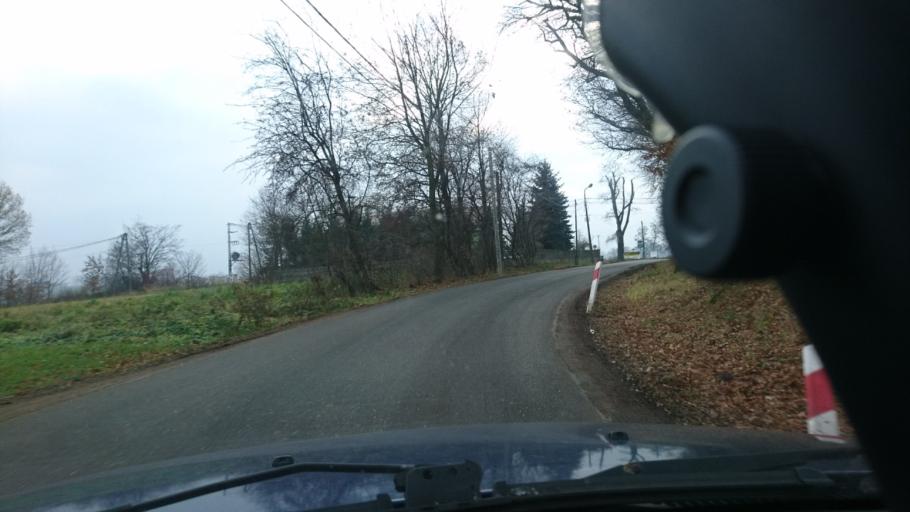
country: PL
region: Silesian Voivodeship
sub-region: Powiat bielski
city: Pisarzowice
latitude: 49.8912
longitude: 19.1483
